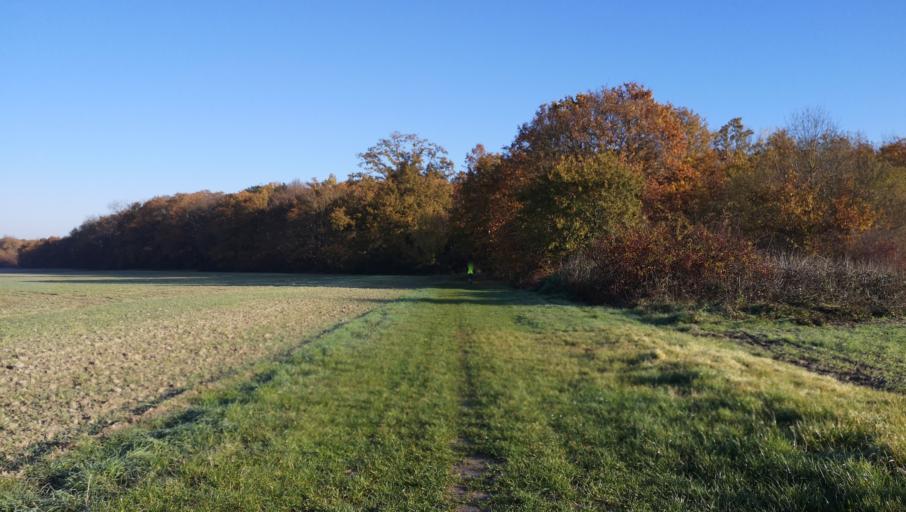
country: FR
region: Centre
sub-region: Departement du Loiret
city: Saran
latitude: 47.9411
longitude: 1.8582
